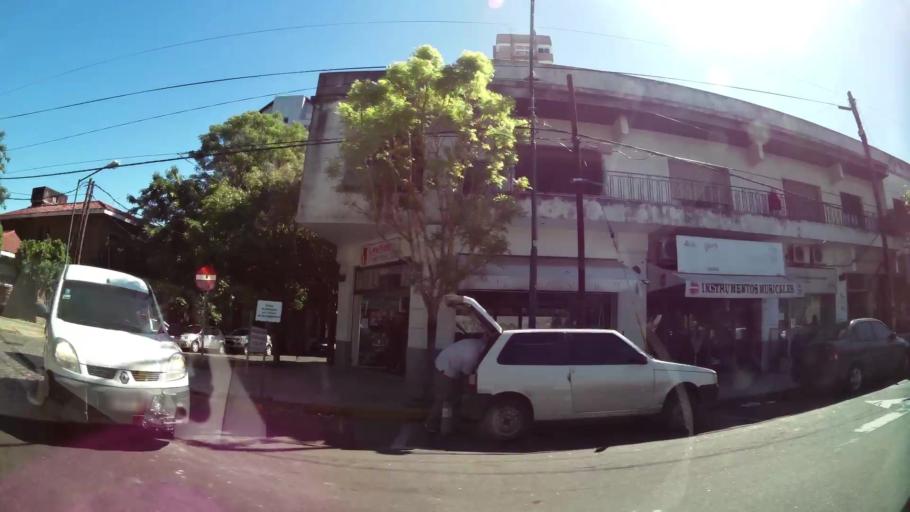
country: AR
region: Buenos Aires
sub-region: Partido de San Isidro
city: San Isidro
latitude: -34.4721
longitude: -58.5138
